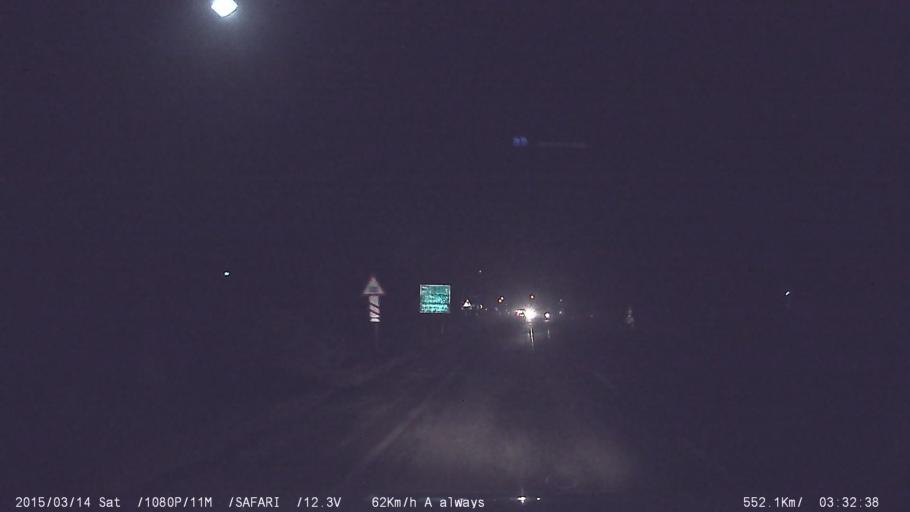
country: IN
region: Kerala
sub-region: Alappuzha
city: Vayalar
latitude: 9.6884
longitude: 76.3299
